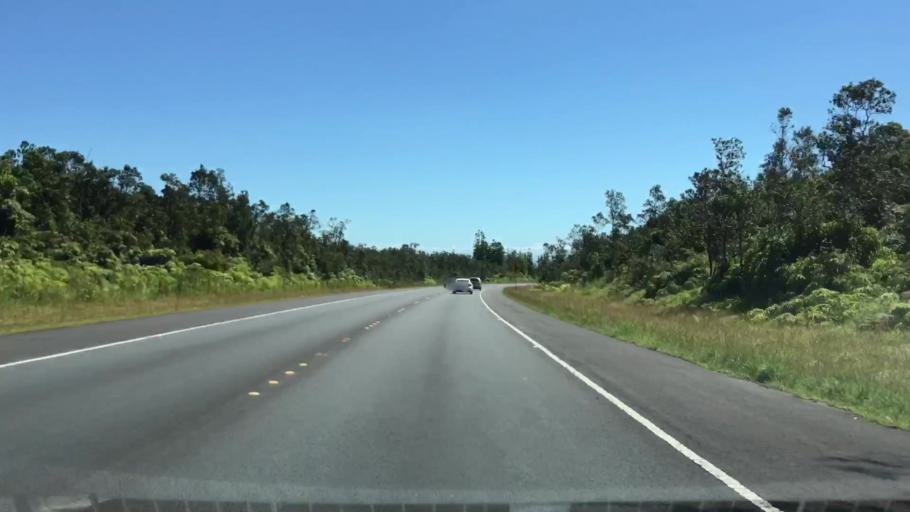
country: US
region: Hawaii
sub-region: Hawaii County
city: Volcano
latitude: 19.4487
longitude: -155.2001
